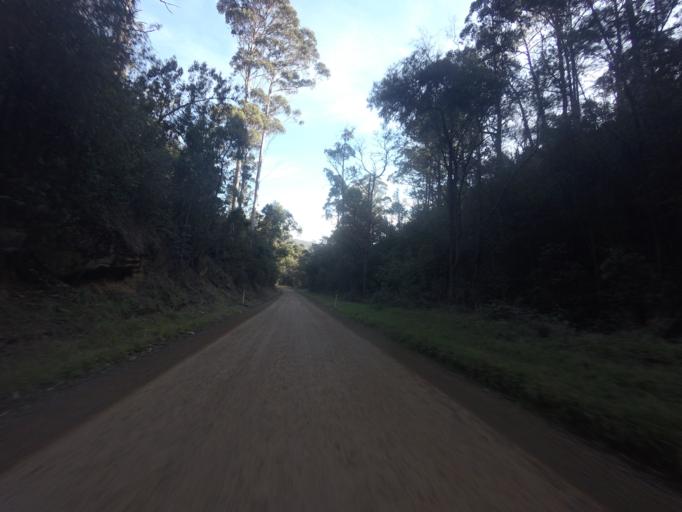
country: AU
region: Tasmania
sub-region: Sorell
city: Sorell
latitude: -42.4855
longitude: 147.4382
